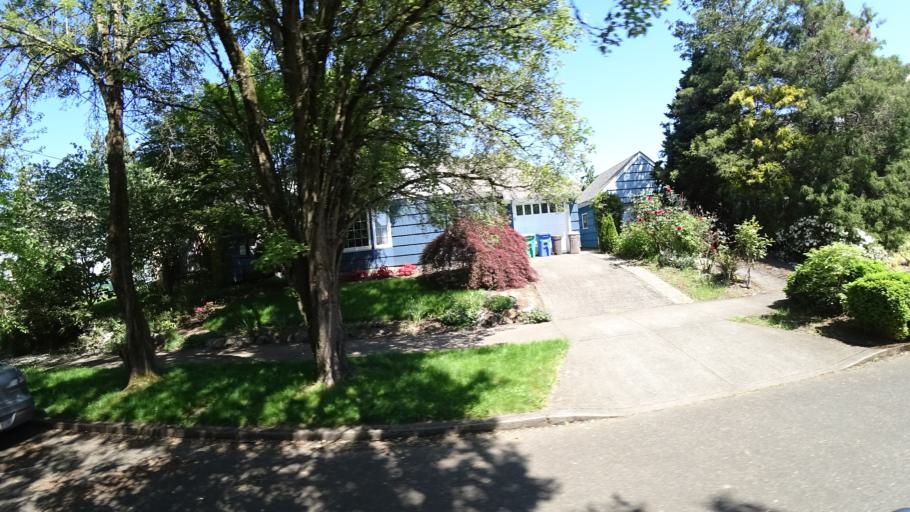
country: US
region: Oregon
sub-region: Multnomah County
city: Portland
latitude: 45.5105
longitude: -122.6368
